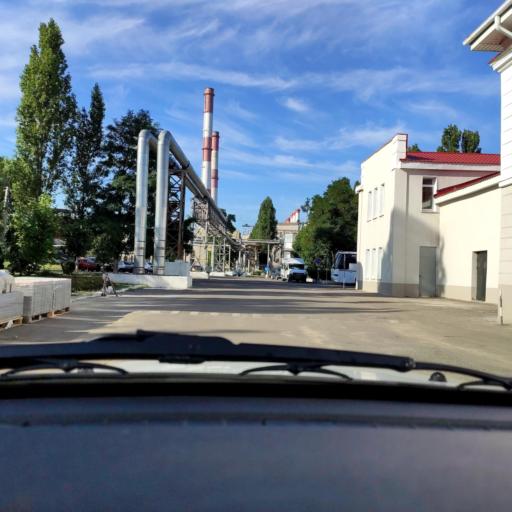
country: RU
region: Voronezj
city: Voronezh
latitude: 51.6300
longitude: 39.2275
